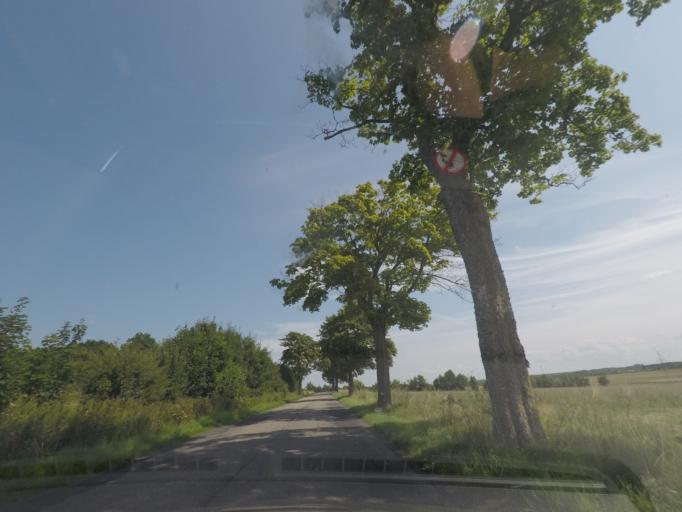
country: PL
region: West Pomeranian Voivodeship
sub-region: Powiat slawienski
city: Darlowo
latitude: 54.4666
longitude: 16.5483
